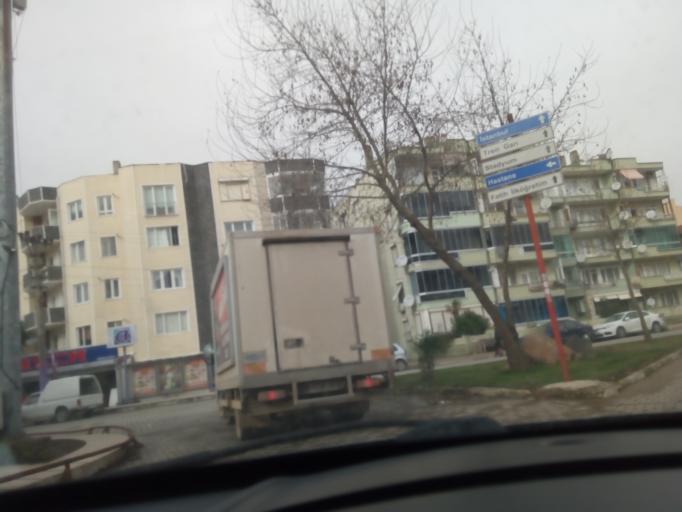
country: TR
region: Balikesir
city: Susurluk
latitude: 39.9183
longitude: 28.1533
